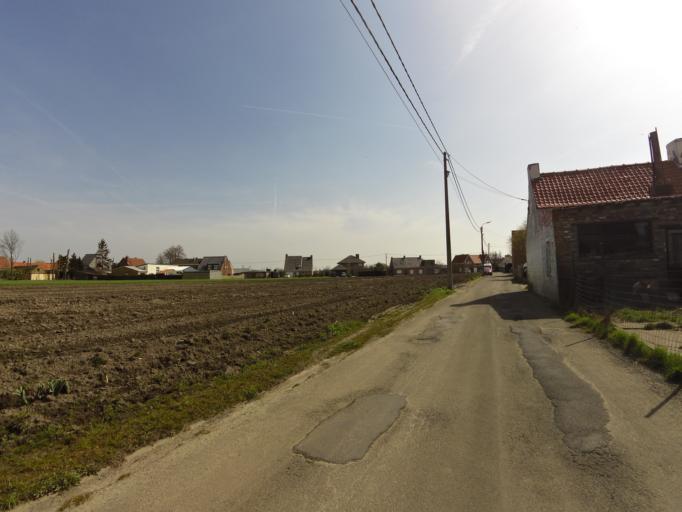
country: BE
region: Flanders
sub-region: Provincie West-Vlaanderen
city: Koekelare
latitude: 51.0992
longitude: 2.9655
